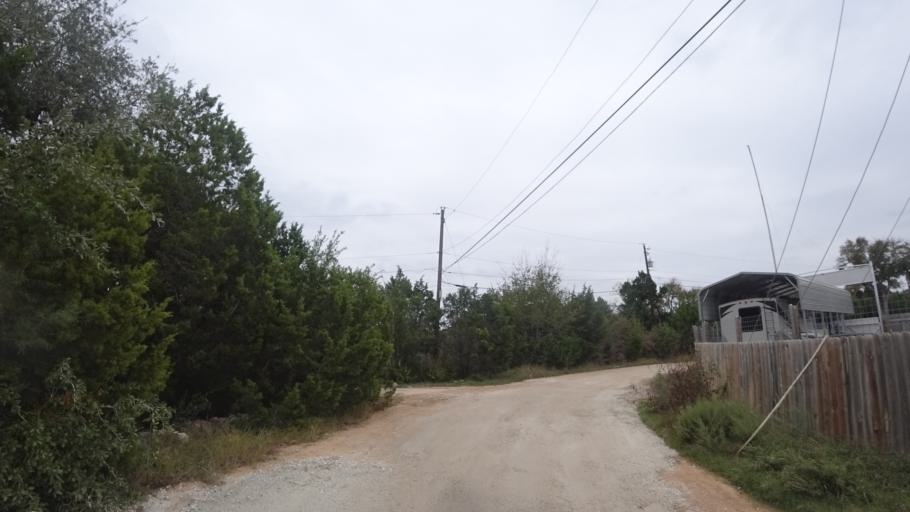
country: US
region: Texas
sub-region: Travis County
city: Hudson Bend
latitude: 30.3849
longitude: -97.9381
